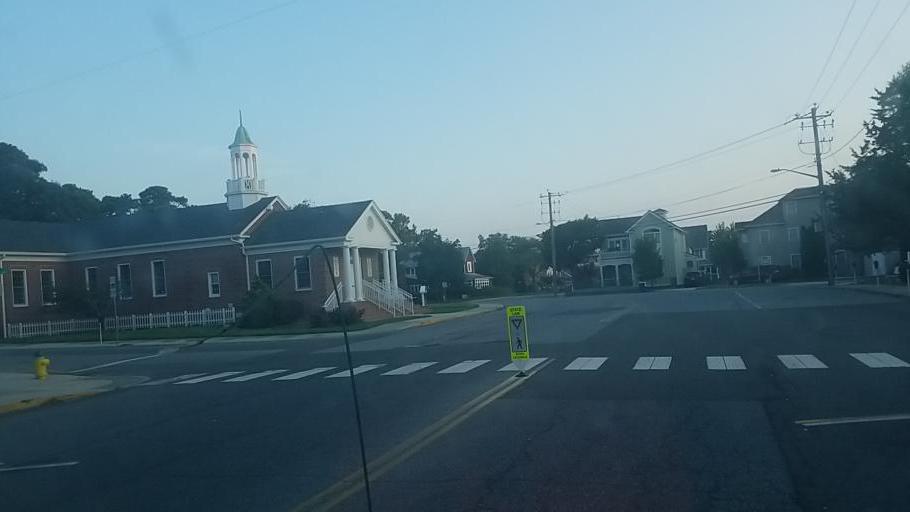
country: US
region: Delaware
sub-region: Sussex County
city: Rehoboth Beach
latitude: 38.7130
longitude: -75.0783
